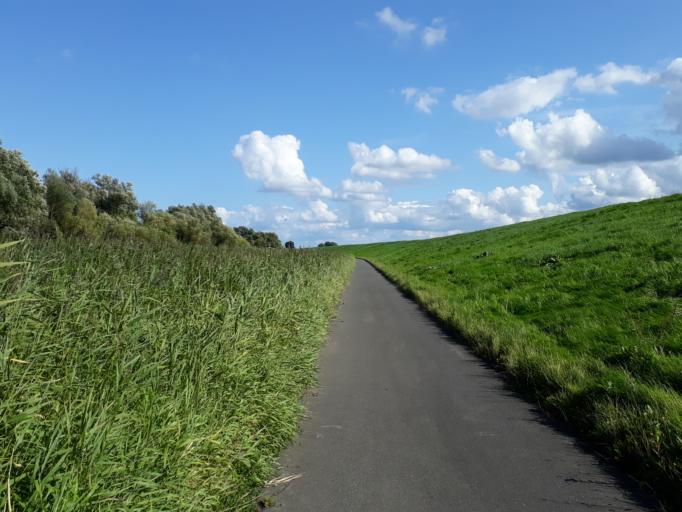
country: DE
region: Lower Saxony
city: Jork
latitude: 53.5507
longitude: 9.6756
